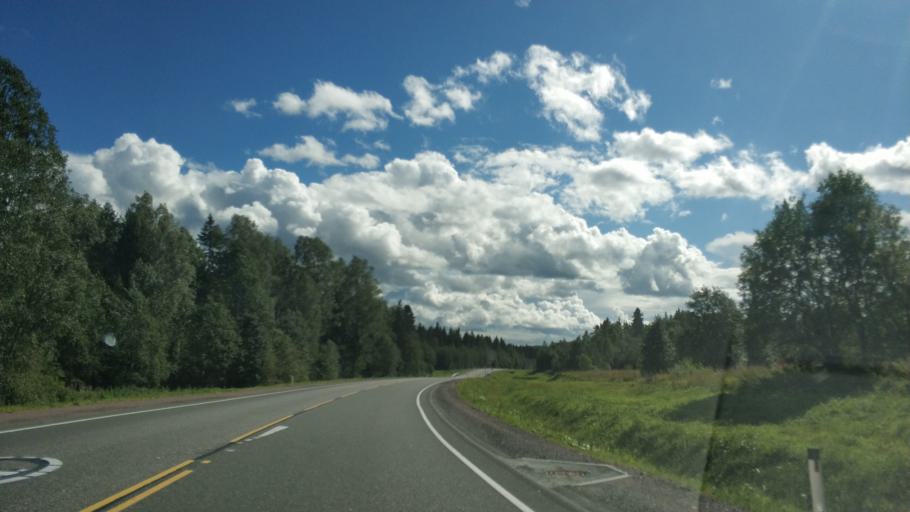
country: RU
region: Republic of Karelia
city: Ruskeala
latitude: 61.8932
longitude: 30.6414
